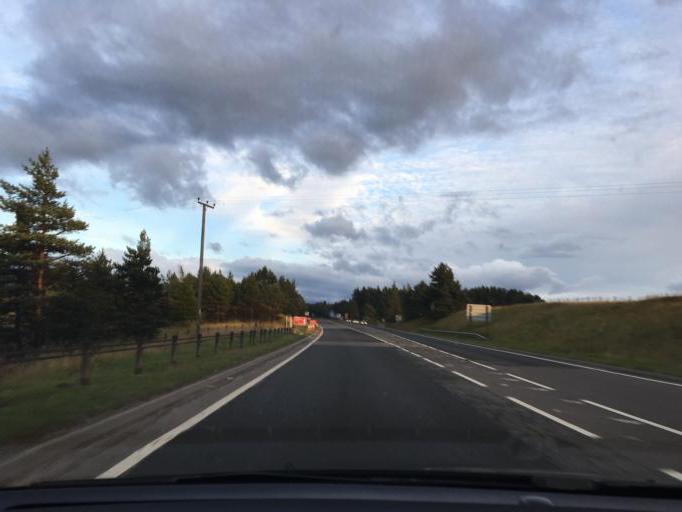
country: GB
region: Scotland
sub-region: Highland
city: Aviemore
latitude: 57.3444
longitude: -4.0006
